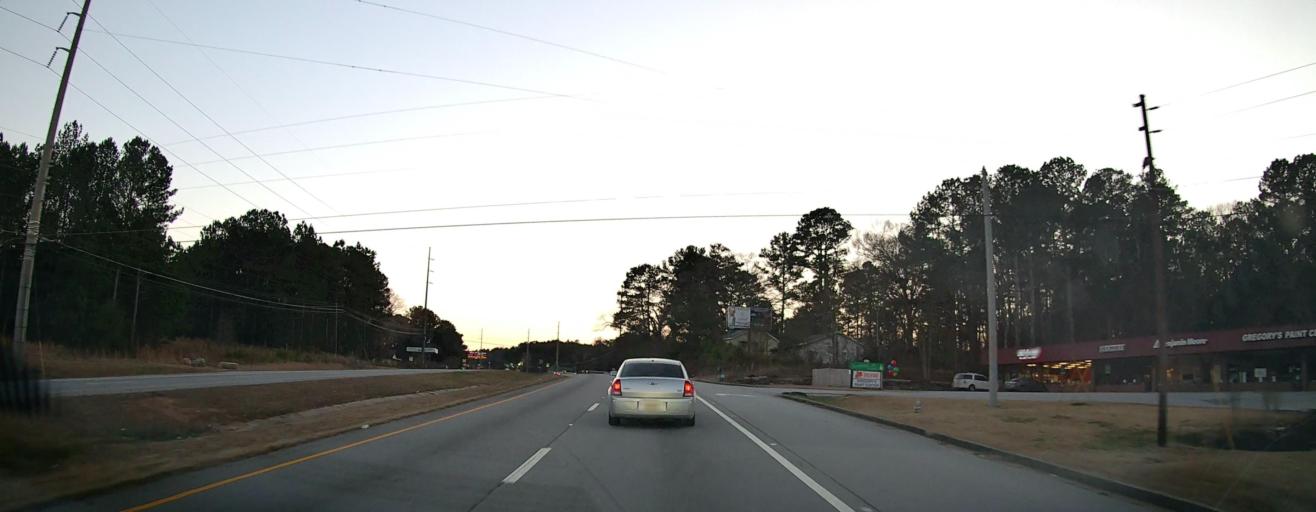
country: US
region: Georgia
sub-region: Clayton County
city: Riverdale
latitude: 33.5144
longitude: -84.4291
